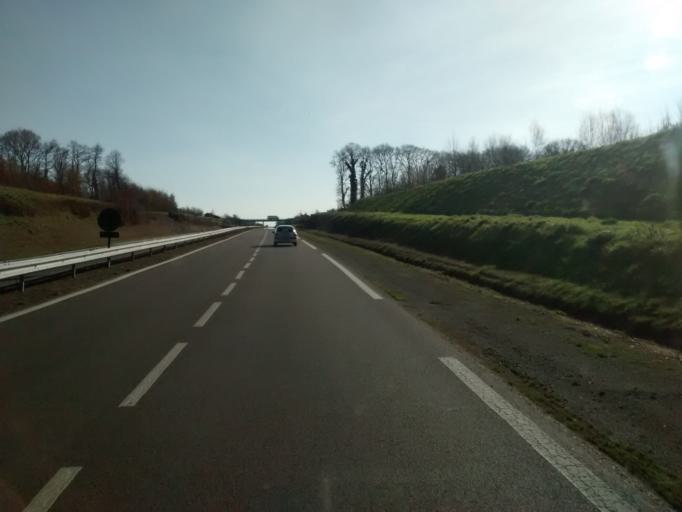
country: FR
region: Brittany
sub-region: Departement d'Ille-et-Vilaine
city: Betton
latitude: 48.1842
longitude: -1.6246
